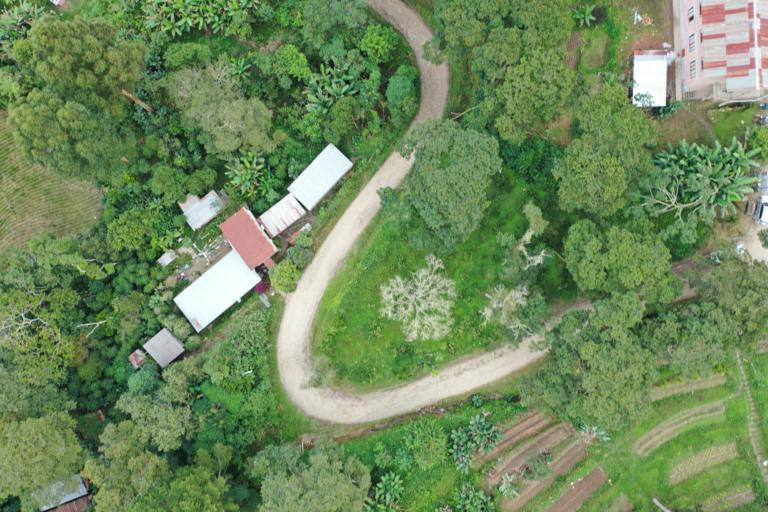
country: BO
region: La Paz
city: Coroico
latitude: -16.2586
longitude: -67.6907
